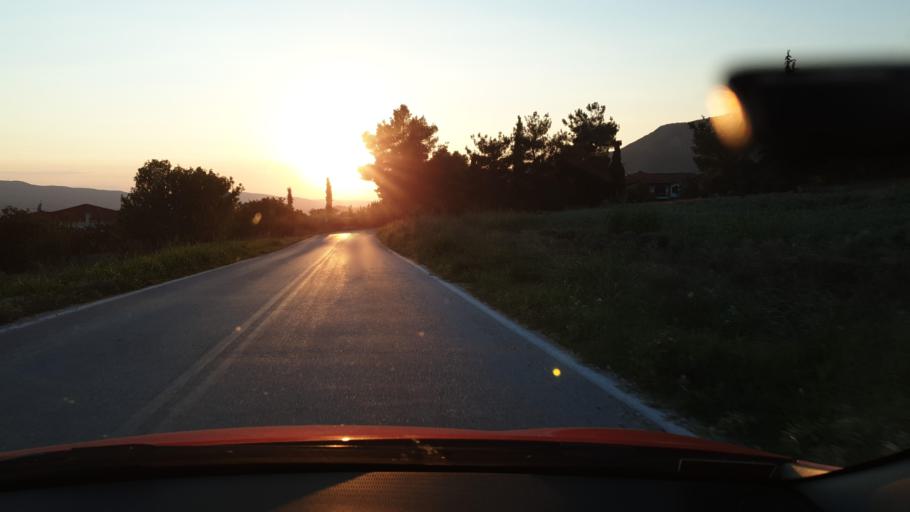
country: GR
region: Central Macedonia
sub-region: Nomos Chalkidikis
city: Galatista
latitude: 40.4679
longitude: 23.2611
